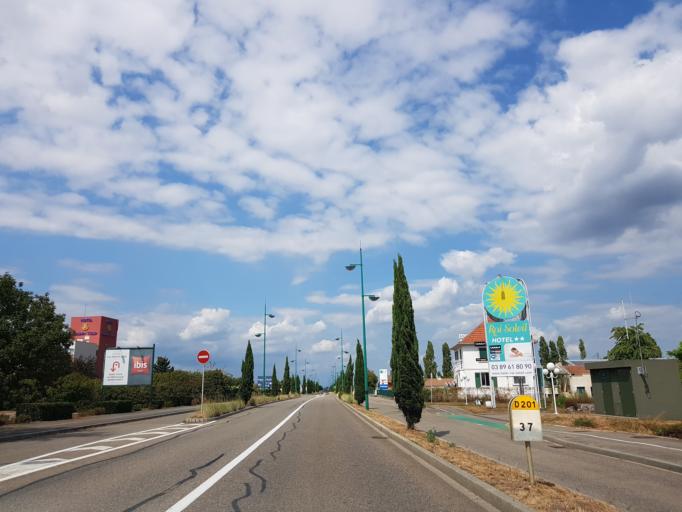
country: FR
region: Alsace
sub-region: Departement du Haut-Rhin
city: Sausheim
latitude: 47.7812
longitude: 7.3889
